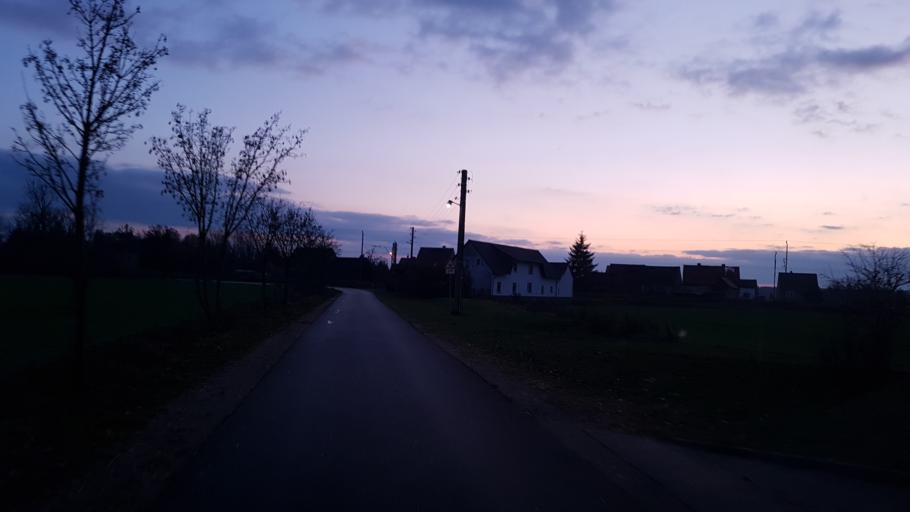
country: DE
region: Brandenburg
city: Falkenberg
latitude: 51.6275
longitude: 13.2021
